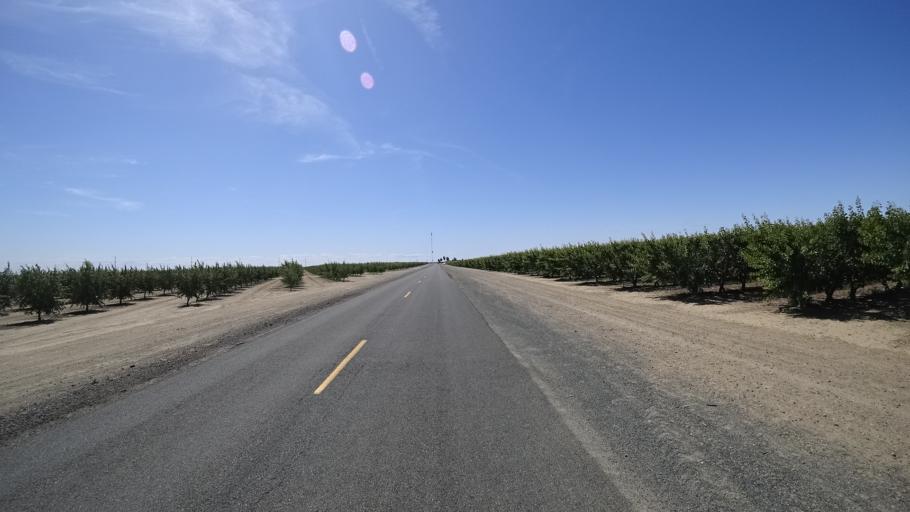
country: US
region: California
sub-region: Kings County
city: Kettleman City
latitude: 35.9410
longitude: -119.9278
